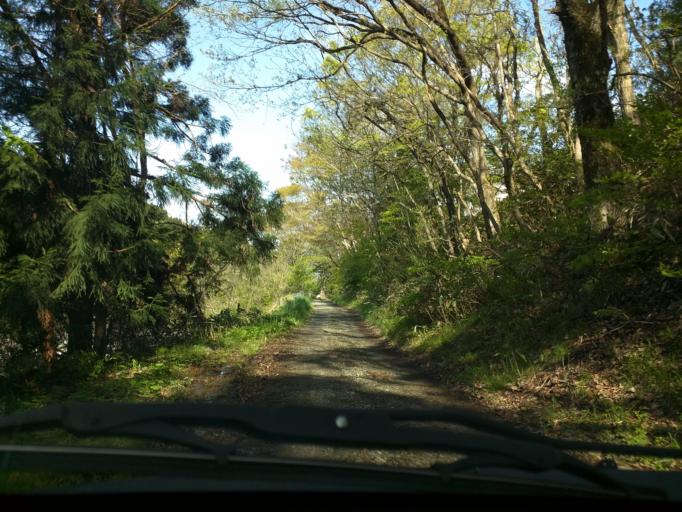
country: JP
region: Fukushima
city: Inawashiro
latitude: 37.5058
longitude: 139.9599
